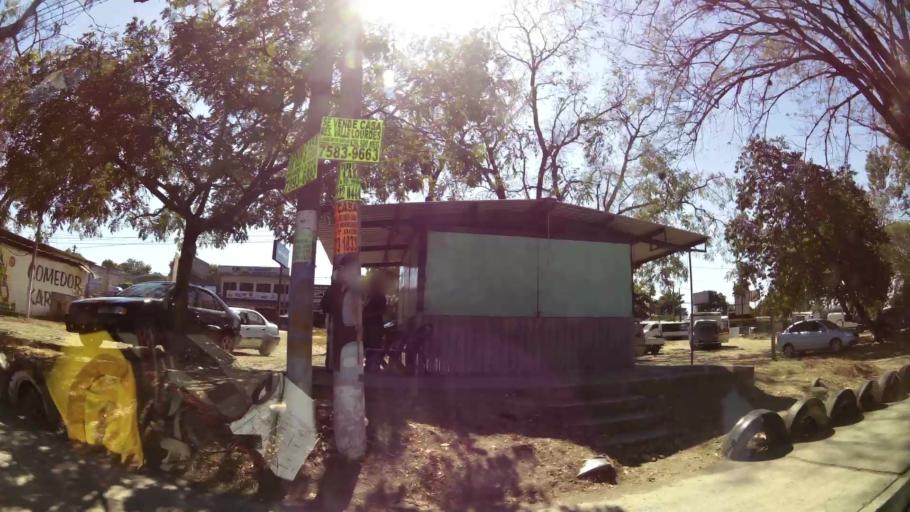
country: SV
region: La Libertad
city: Santa Tecla
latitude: 13.7238
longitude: -89.3694
